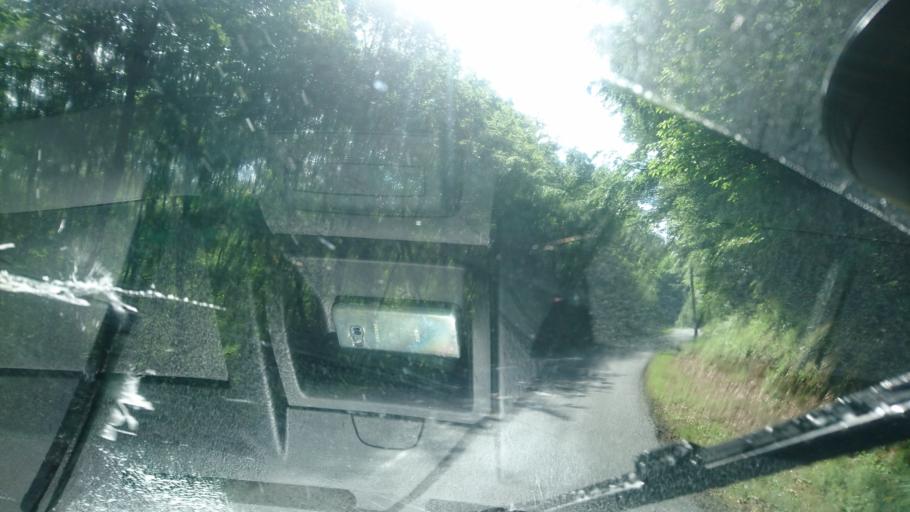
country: FR
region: Limousin
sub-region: Departement de la Haute-Vienne
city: Peyrat-le-Chateau
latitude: 45.8088
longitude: 1.8165
